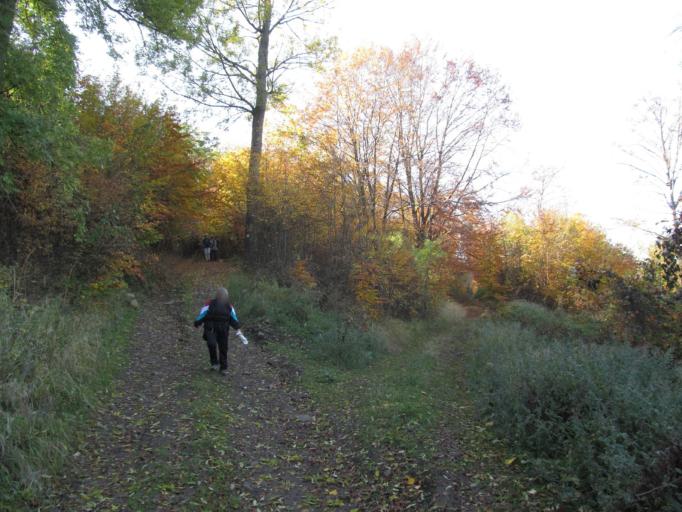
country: SK
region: Nitriansky
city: Sahy
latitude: 47.9721
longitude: 18.9376
